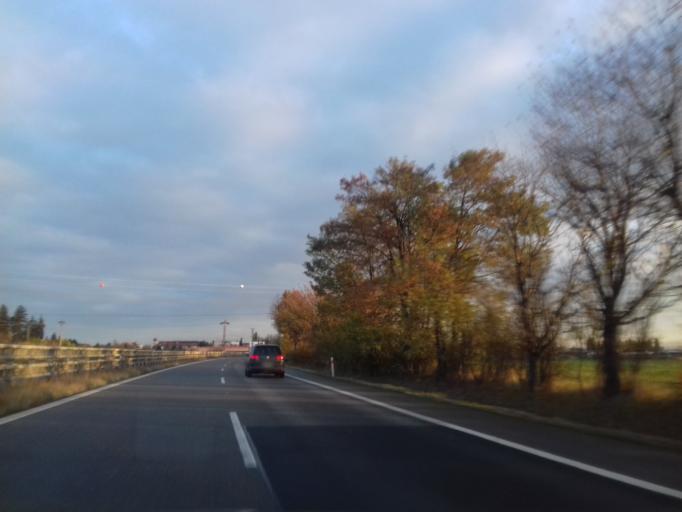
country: CZ
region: Olomoucky
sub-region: Okres Prostejov
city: Prostejov
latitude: 49.4585
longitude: 17.1172
